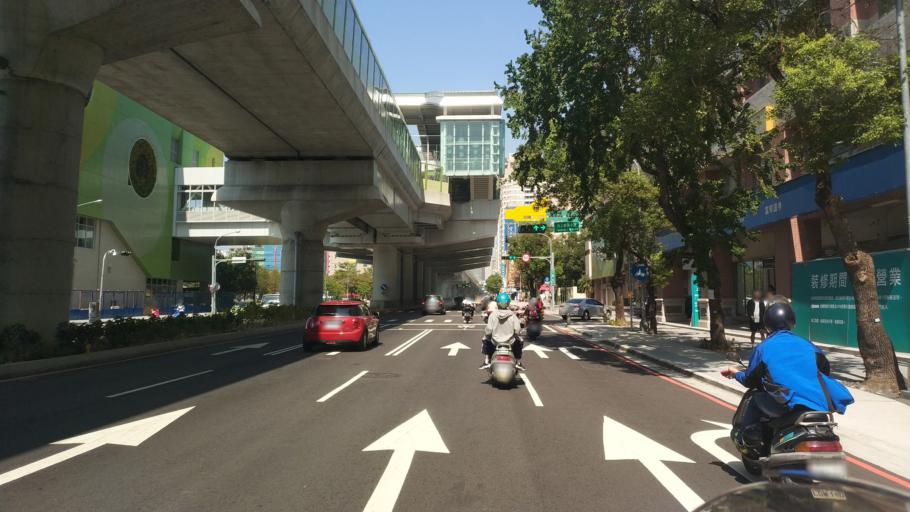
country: TW
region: Taiwan
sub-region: Taichung City
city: Taichung
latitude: 24.1444
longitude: 120.6468
